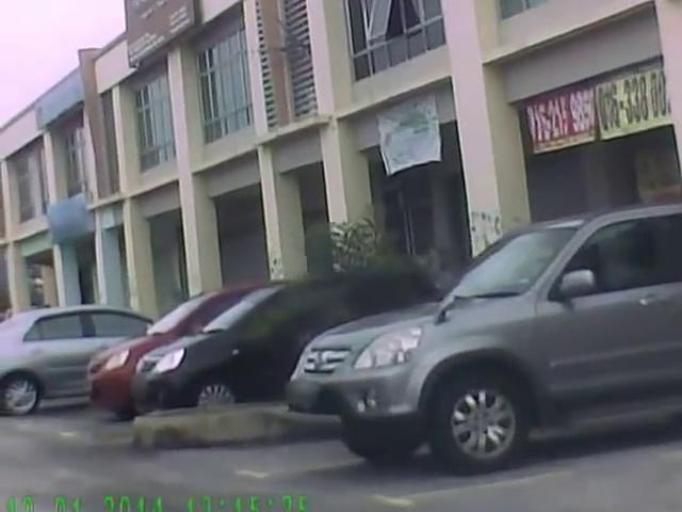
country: MY
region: Selangor
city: Klang
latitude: 3.0667
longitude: 101.4739
